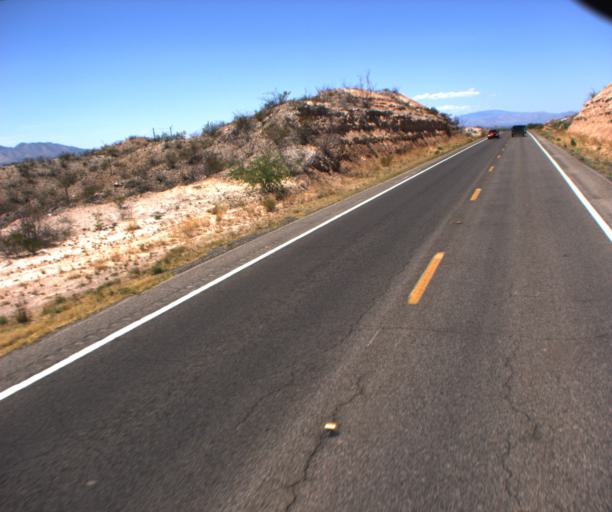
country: US
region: Arizona
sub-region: Cochise County
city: Saint David
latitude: 31.8257
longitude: -110.1768
